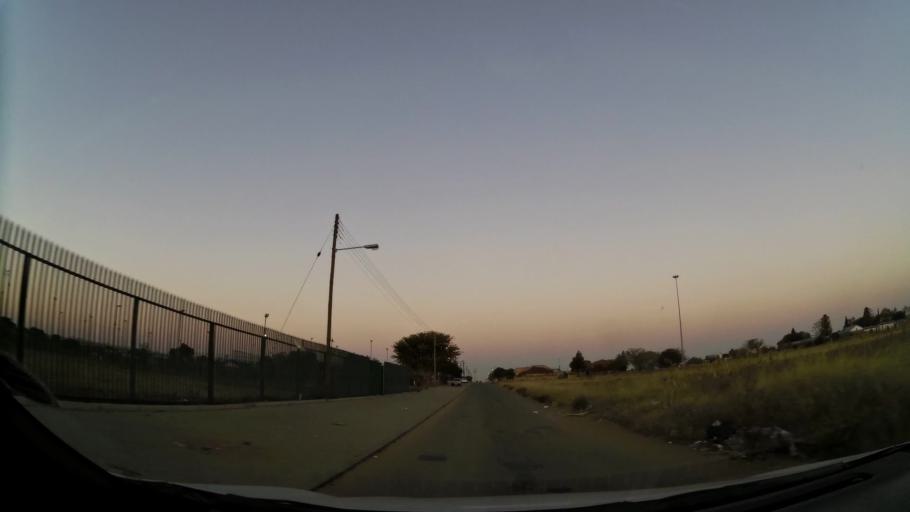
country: ZA
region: Limpopo
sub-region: Capricorn District Municipality
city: Polokwane
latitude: -23.8560
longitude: 29.3893
